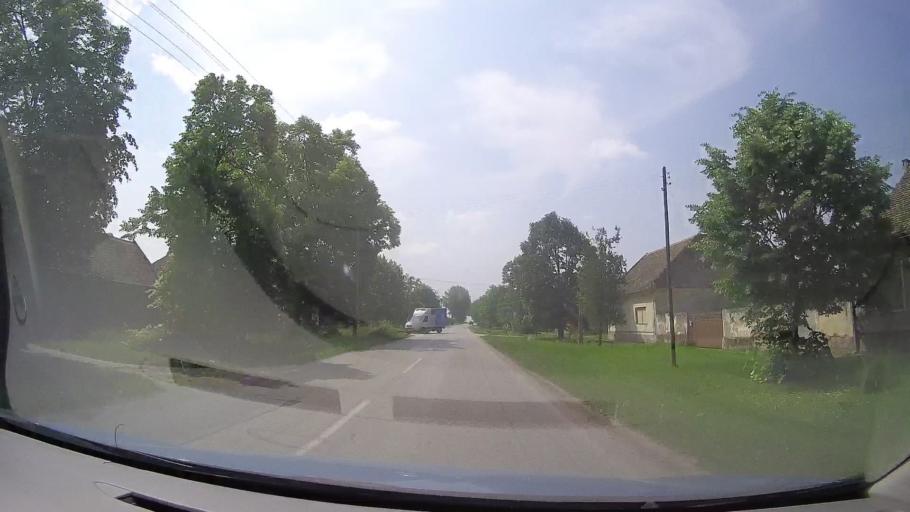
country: RS
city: Crepaja
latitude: 45.0035
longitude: 20.6388
